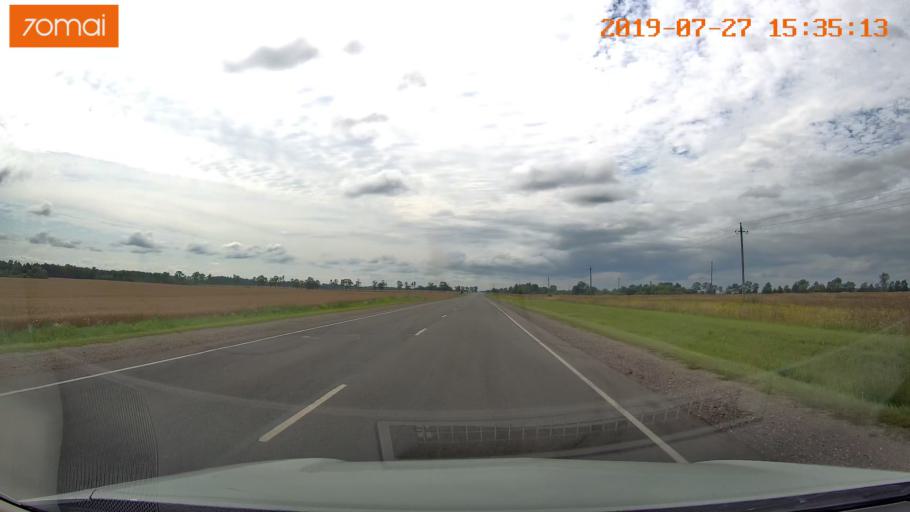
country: RU
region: Kaliningrad
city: Nesterov
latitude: 54.6140
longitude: 22.4031
